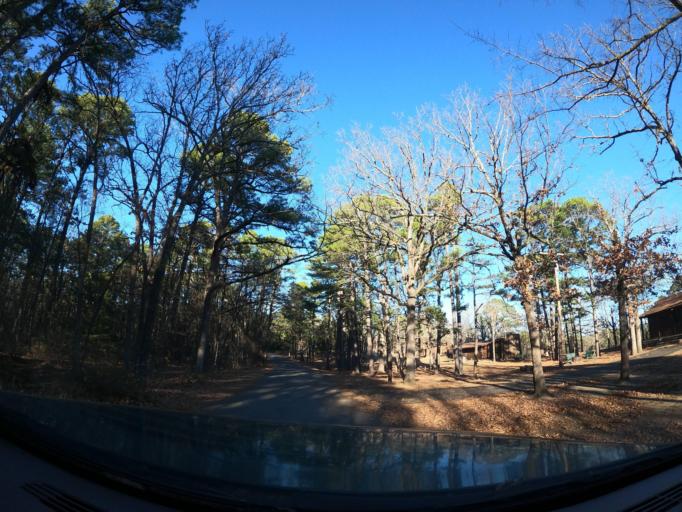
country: US
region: Oklahoma
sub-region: Latimer County
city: Wilburton
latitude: 34.9786
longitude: -95.3526
